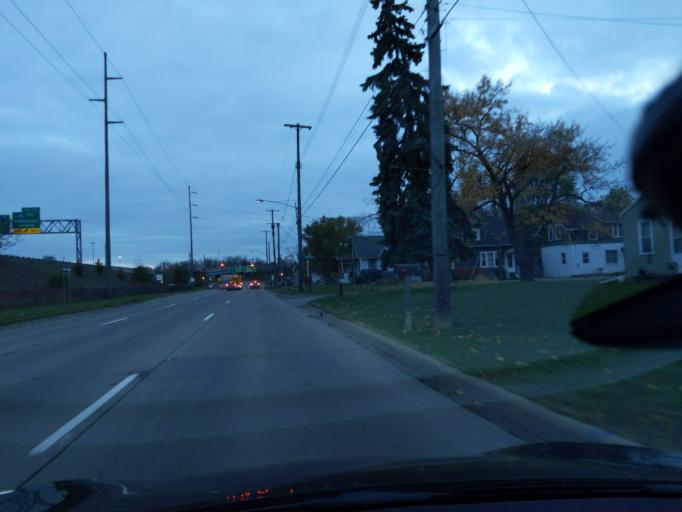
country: US
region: Michigan
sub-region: Ingham County
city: East Lansing
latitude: 42.7313
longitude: -84.5112
